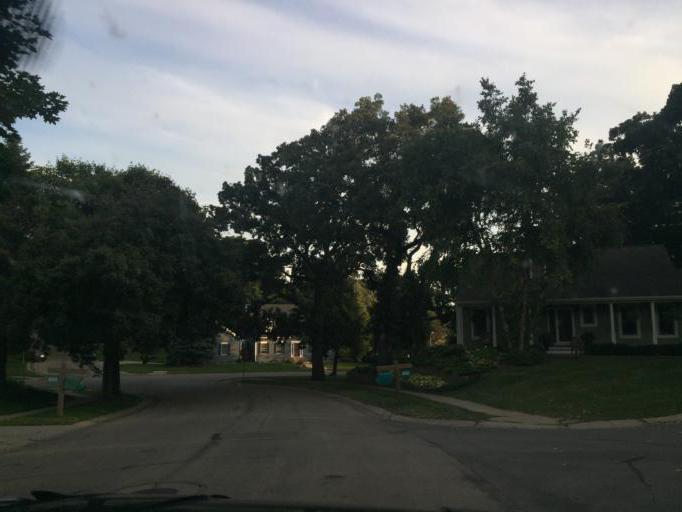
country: US
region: Minnesota
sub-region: Olmsted County
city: Rochester
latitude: 44.0092
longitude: -92.5069
